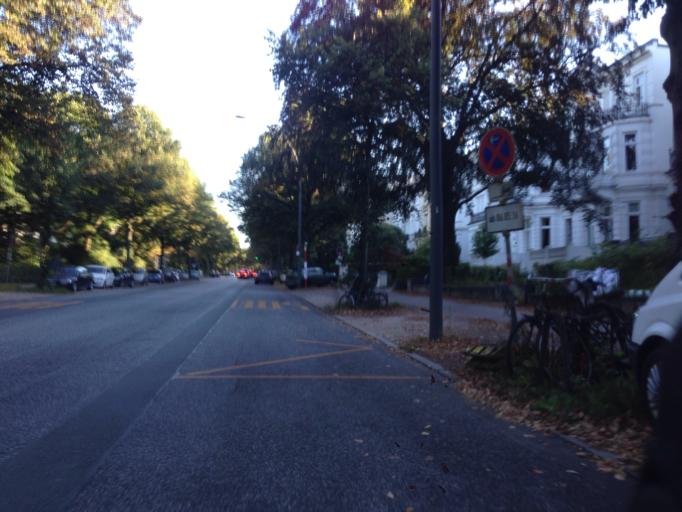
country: DE
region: Hamburg
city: Hamburg-Nord
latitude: 53.5806
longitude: 9.9887
